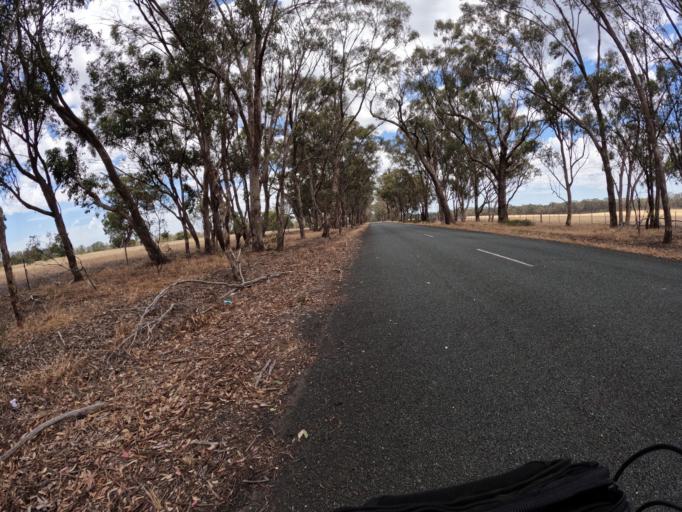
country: AU
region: Victoria
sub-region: Greater Shepparton
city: Shepparton
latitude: -36.6808
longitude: 145.1932
